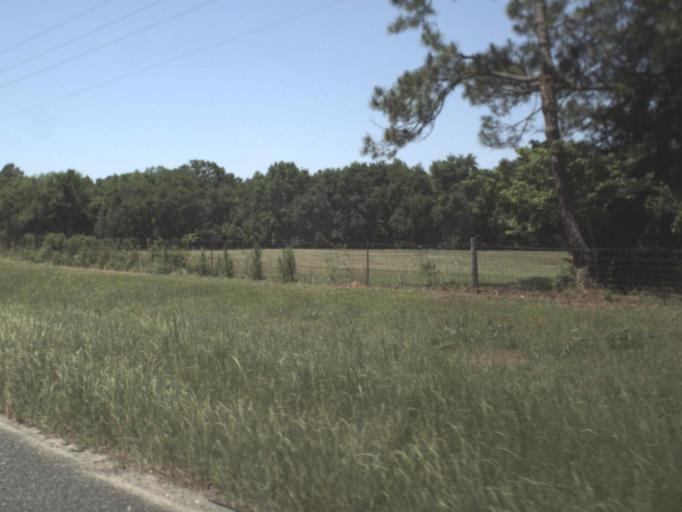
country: US
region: Florida
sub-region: Jefferson County
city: Monticello
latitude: 30.4436
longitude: -83.9019
